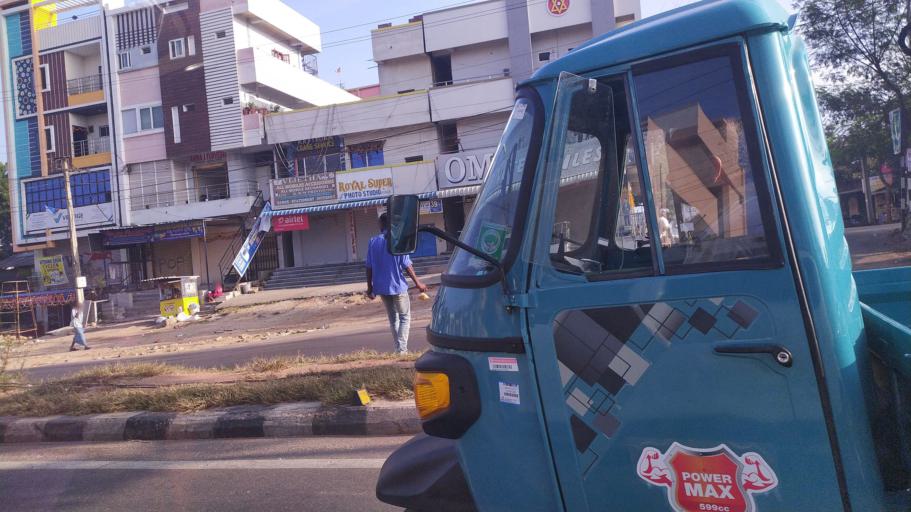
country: IN
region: Telangana
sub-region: Rangareddi
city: Balapur
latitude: 17.3201
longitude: 78.4341
